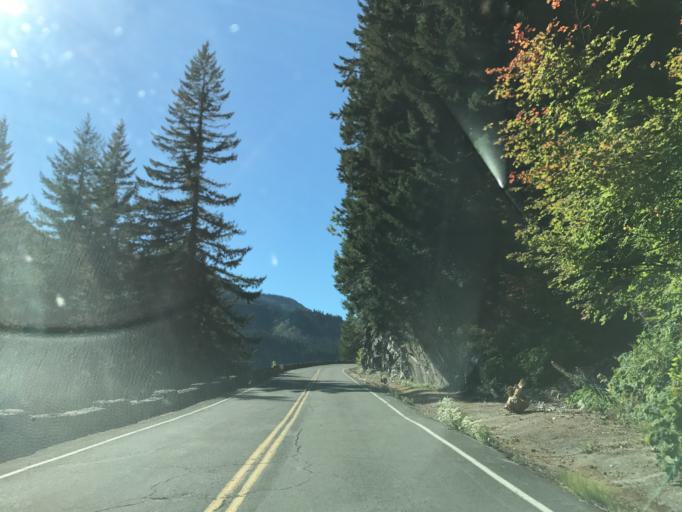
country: US
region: Washington
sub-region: Pierce County
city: Buckley
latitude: 46.7615
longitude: -121.6552
